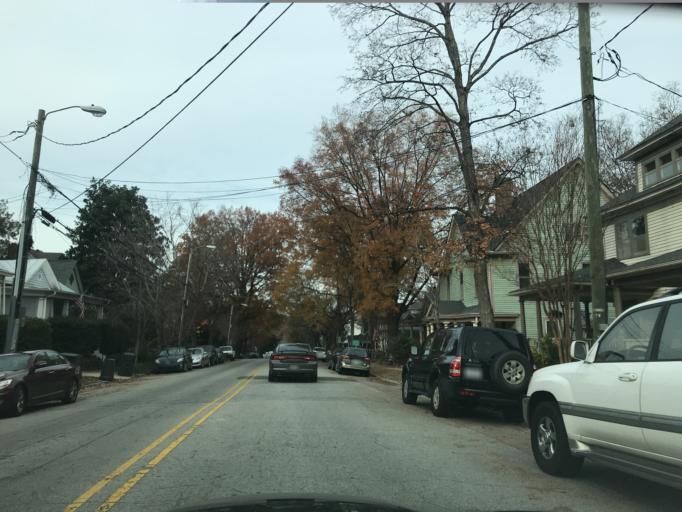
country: US
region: North Carolina
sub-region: Wake County
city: Raleigh
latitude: 35.7812
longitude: -78.6333
